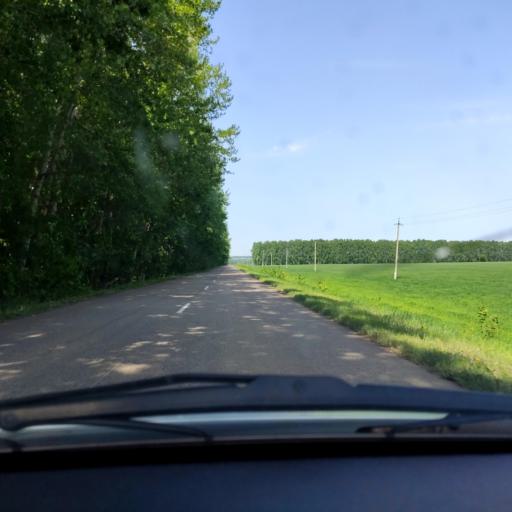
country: RU
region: Bashkortostan
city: Avdon
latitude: 54.5160
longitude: 55.6289
